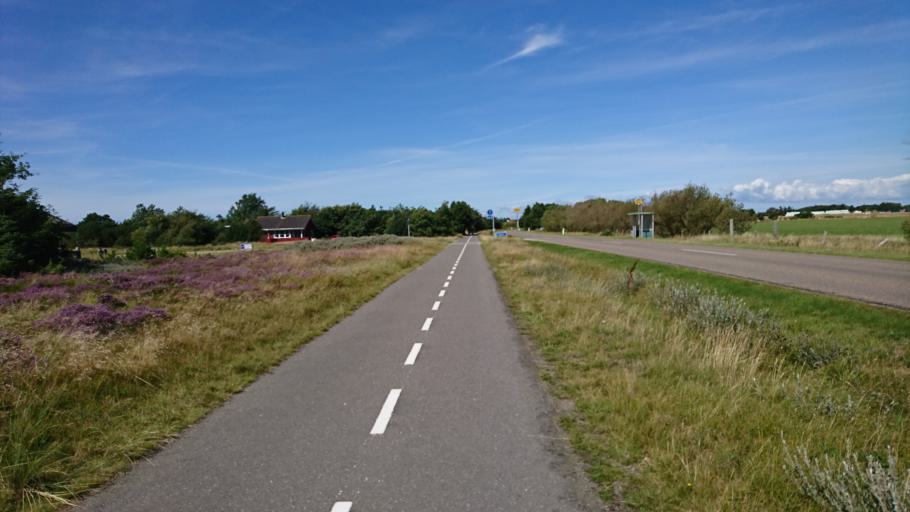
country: DK
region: South Denmark
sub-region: Fano Kommune
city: Nordby
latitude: 55.4165
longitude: 8.4013
